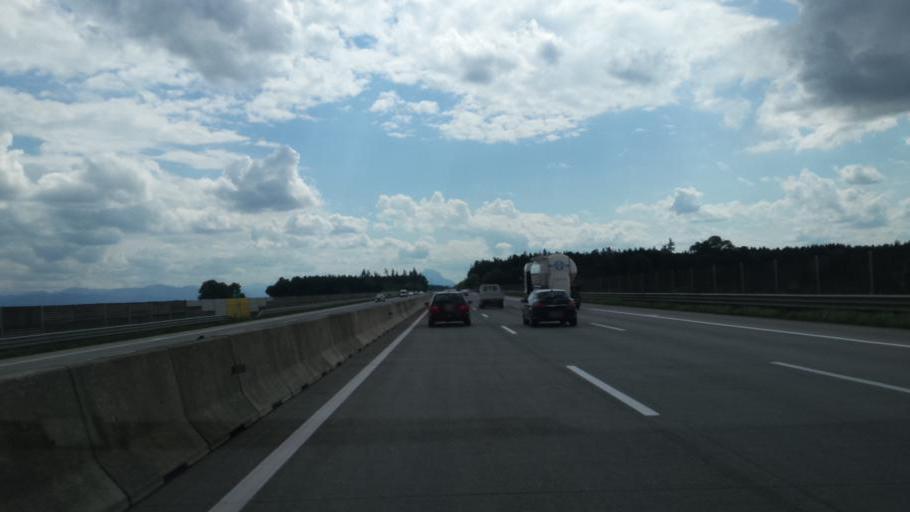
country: AT
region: Upper Austria
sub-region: Wels-Land
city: Marchtrenk
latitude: 48.1269
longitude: 14.1169
